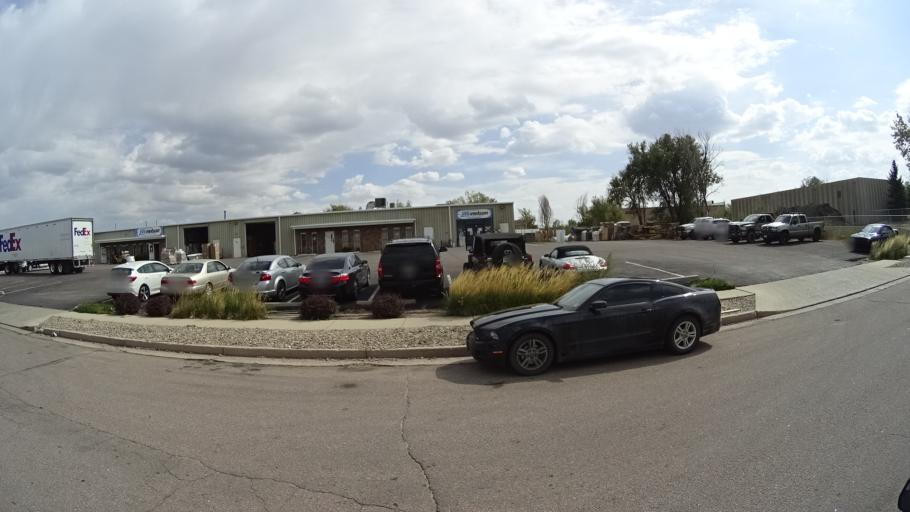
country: US
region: Colorado
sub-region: El Paso County
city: Cimarron Hills
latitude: 38.8430
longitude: -104.7338
